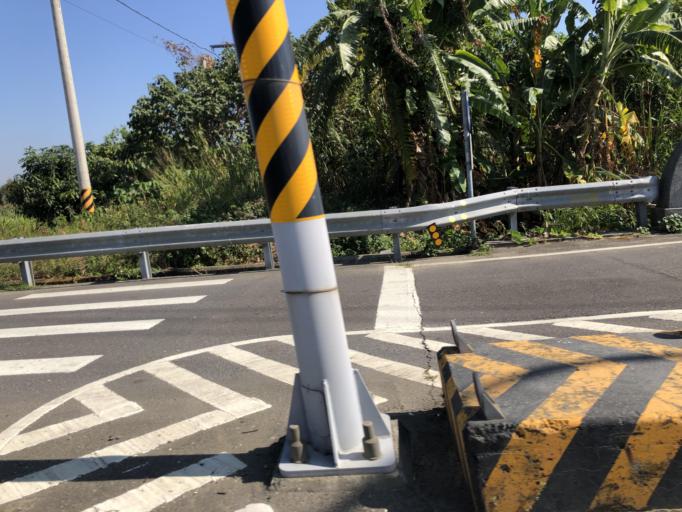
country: TW
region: Taiwan
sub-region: Tainan
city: Tainan
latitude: 23.0358
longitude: 120.3215
